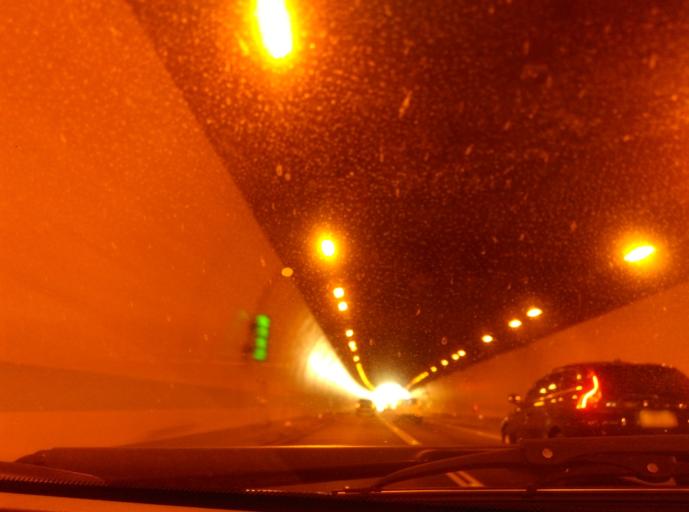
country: TW
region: Taipei
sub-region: Taipei
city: Banqiao
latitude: 24.9777
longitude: 121.5112
